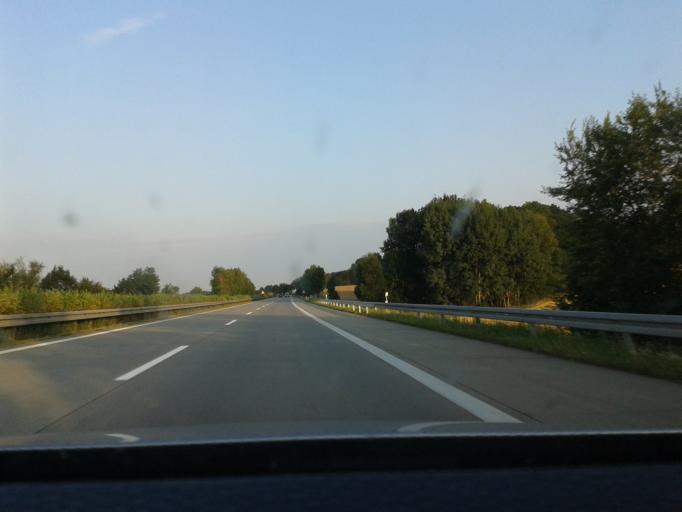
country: DE
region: Saxony
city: Rosswein
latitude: 51.0993
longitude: 13.2105
